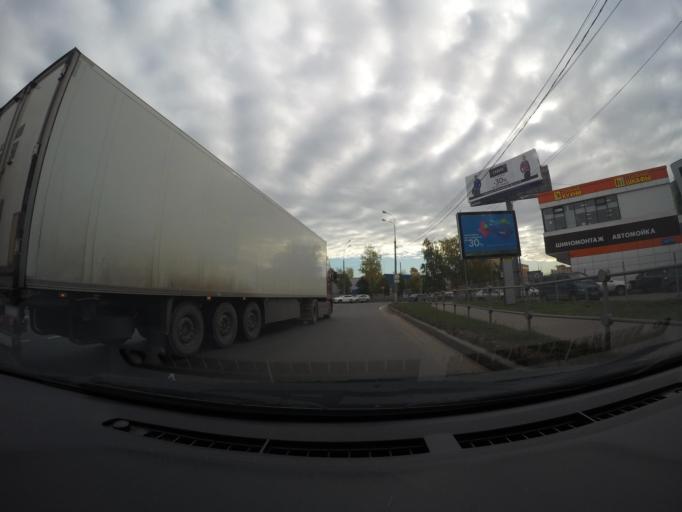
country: RU
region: Moskovskaya
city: Mytishchi
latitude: 55.9322
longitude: 37.7521
